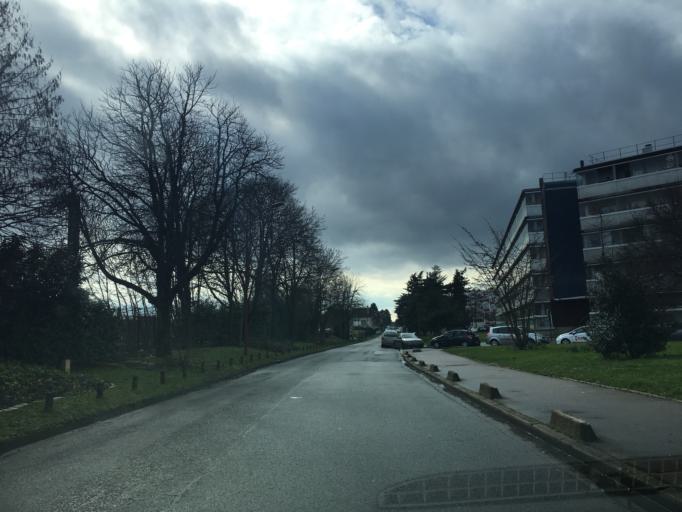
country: FR
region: Ile-de-France
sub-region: Departement du Val-d'Oise
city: Arnouville
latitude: 49.0015
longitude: 2.4277
